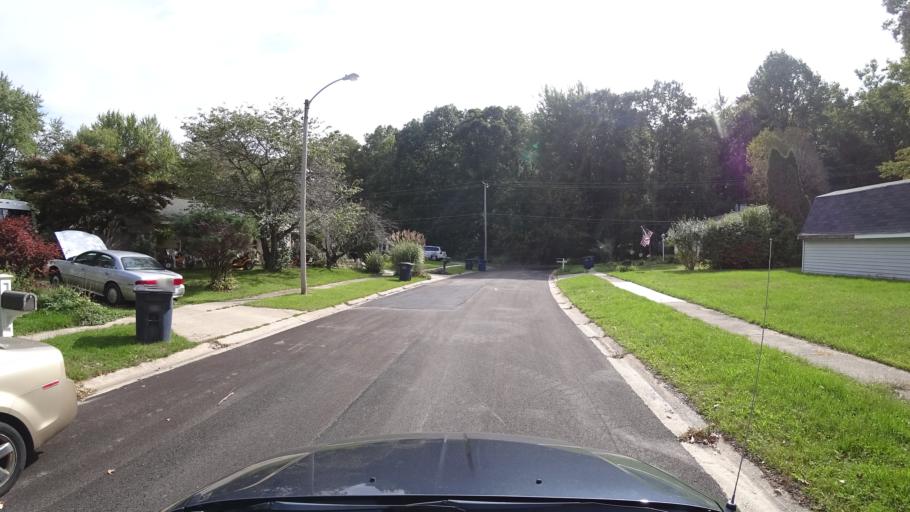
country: US
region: Indiana
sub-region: LaPorte County
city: Trail Creek
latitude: 41.7170
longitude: -86.8309
